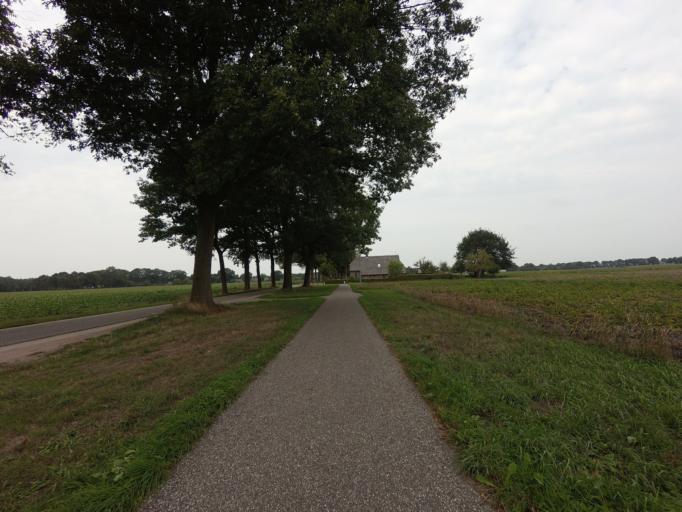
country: NL
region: Drenthe
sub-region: Gemeente Assen
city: Assen
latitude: 52.9922
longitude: 6.6387
